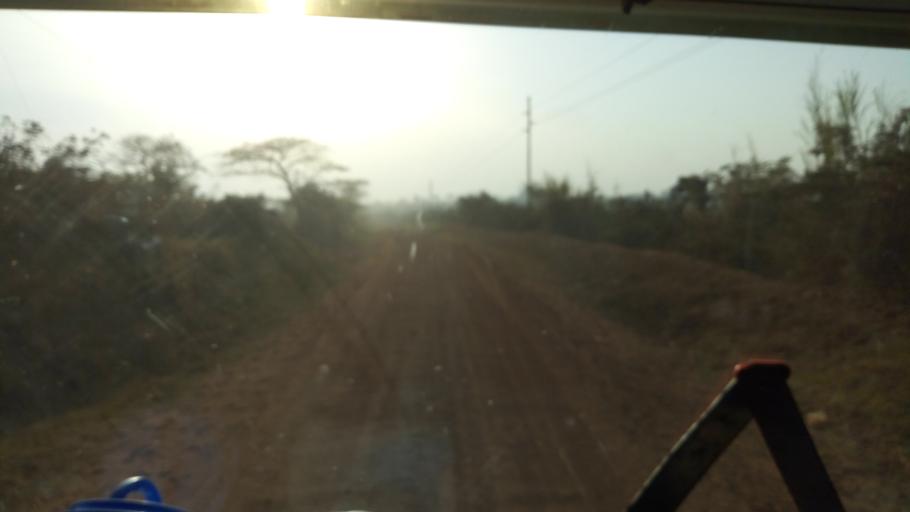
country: UG
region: Western Region
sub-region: Kiryandongo District
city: Kiryandongo
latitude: 1.7928
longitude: 31.9162
